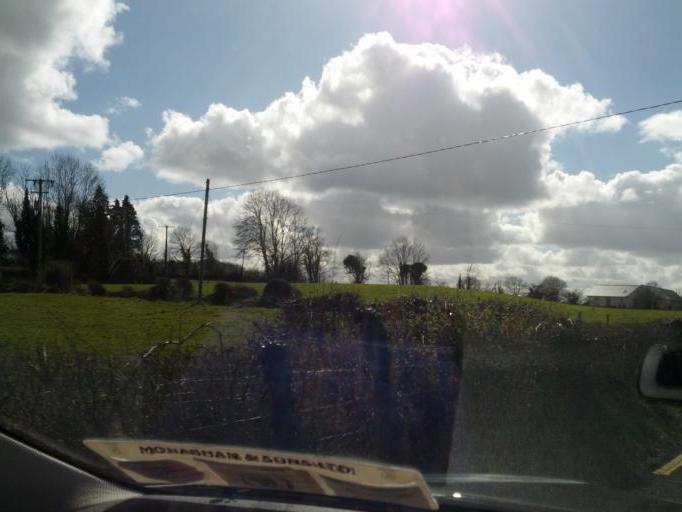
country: IE
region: Connaught
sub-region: County Galway
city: Athenry
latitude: 53.4082
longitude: -8.6334
